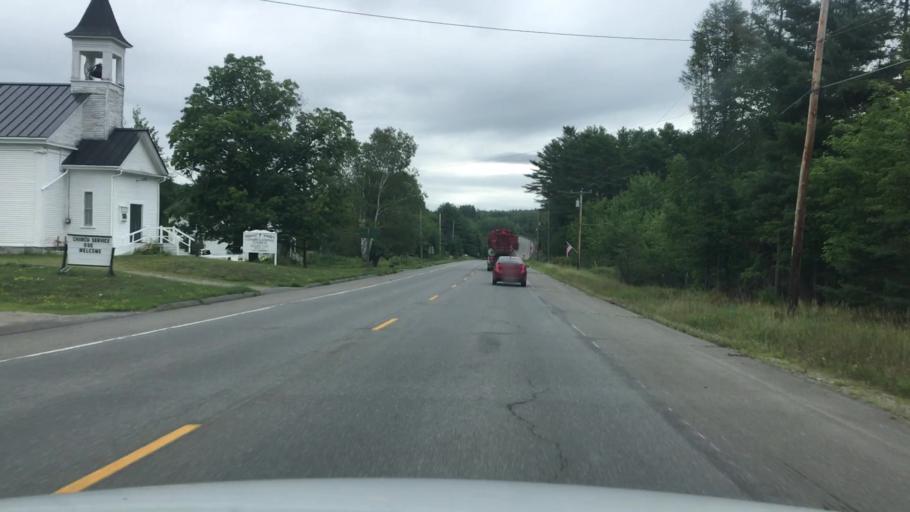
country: US
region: Maine
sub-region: Hancock County
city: Franklin
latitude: 44.8333
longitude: -68.3615
